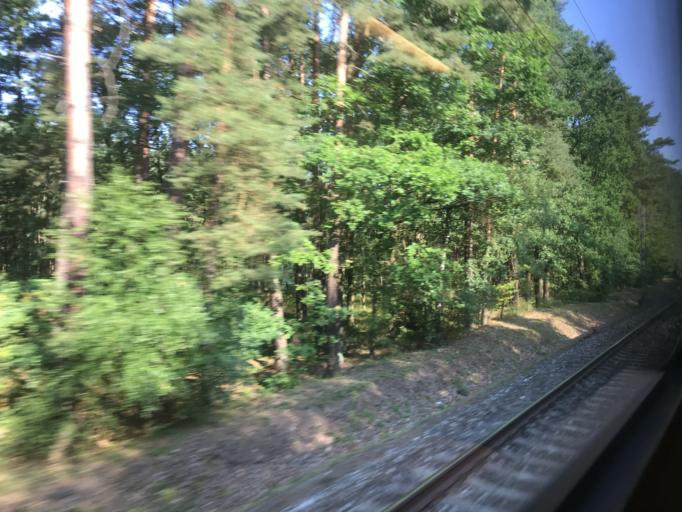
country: CZ
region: Jihocesky
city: Plana nad Luznici
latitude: 49.3298
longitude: 14.7148
